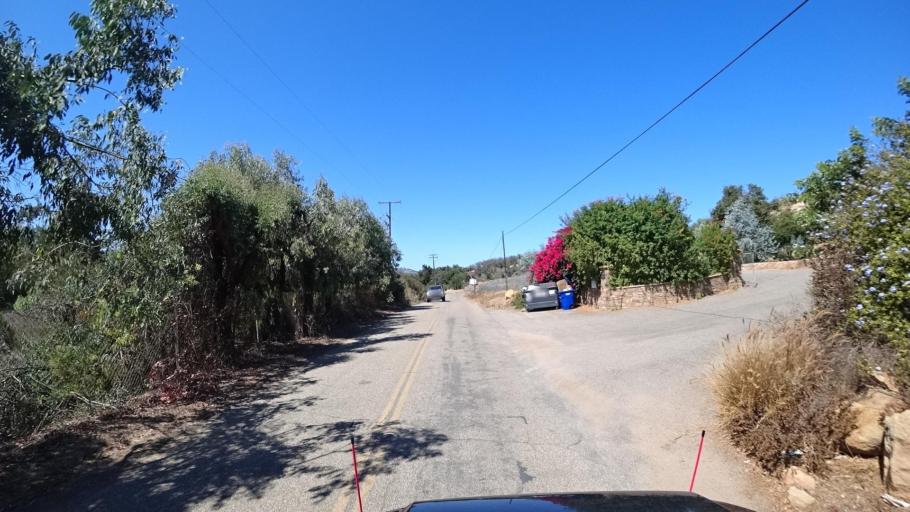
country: US
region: California
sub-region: San Diego County
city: Hidden Meadows
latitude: 33.2411
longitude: -117.0785
